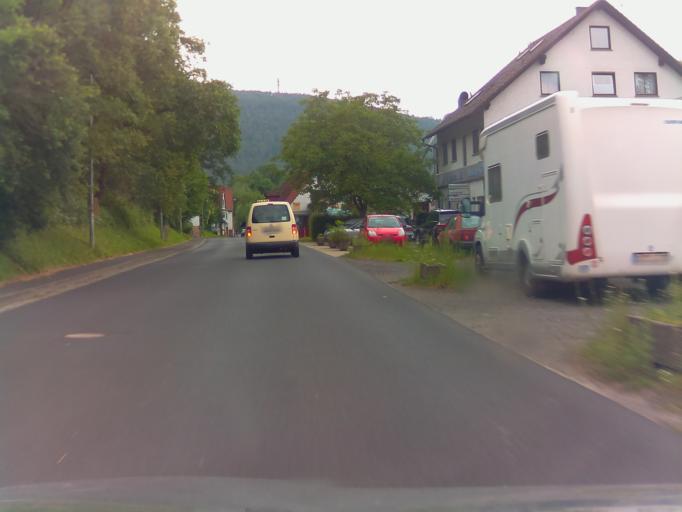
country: DE
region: Bavaria
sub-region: Regierungsbezirk Unterfranken
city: Gemunden
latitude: 50.0607
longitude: 9.6958
